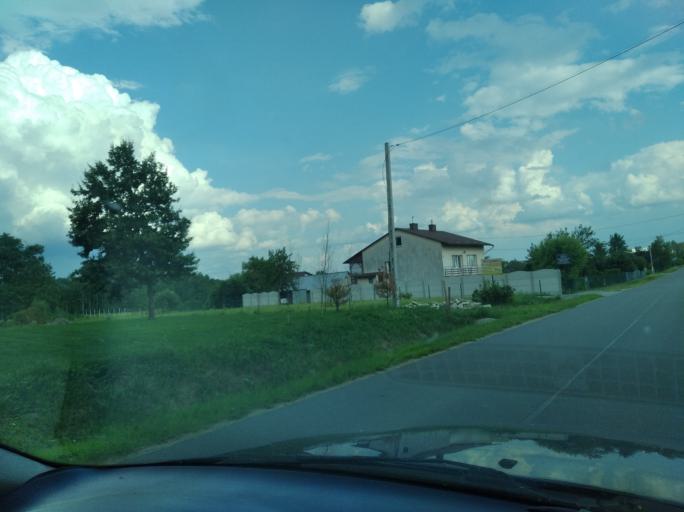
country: PL
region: Subcarpathian Voivodeship
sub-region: Powiat rzeszowski
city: Wysoka Glogowska
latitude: 50.1288
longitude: 22.0247
